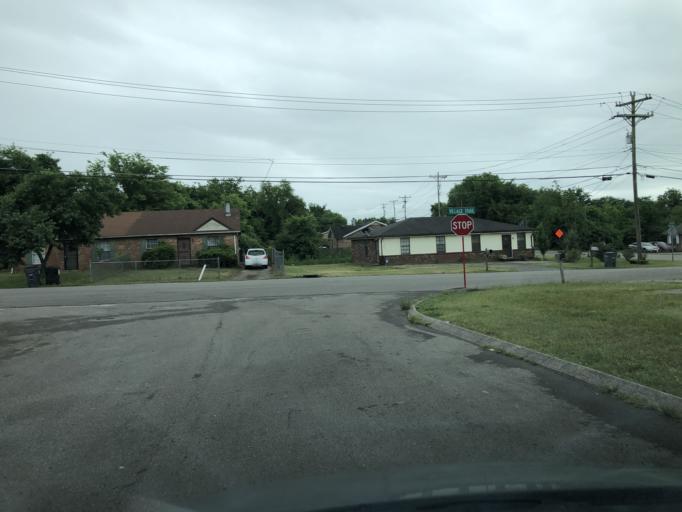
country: US
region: Tennessee
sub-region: Davidson County
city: Nashville
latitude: 36.2479
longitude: -86.7725
